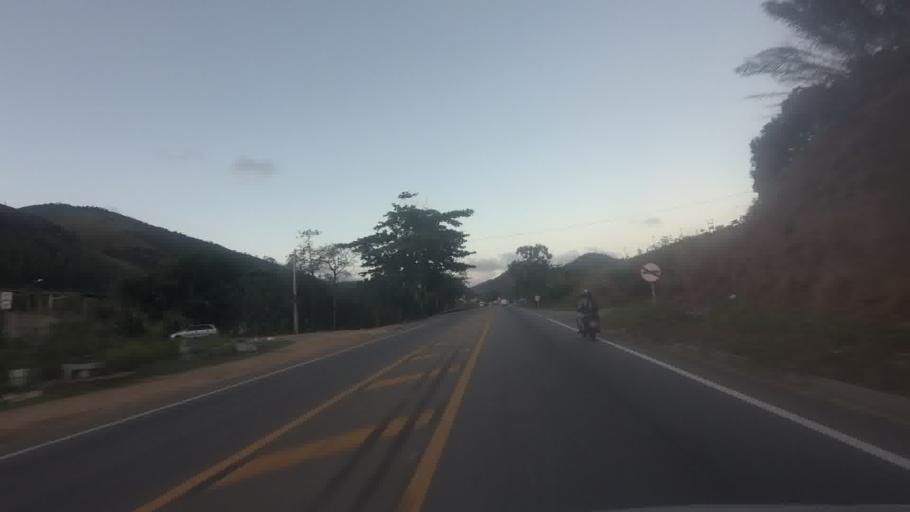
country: BR
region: Espirito Santo
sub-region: Rio Novo Do Sul
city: Rio Novo do Sul
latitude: -20.8687
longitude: -40.9406
